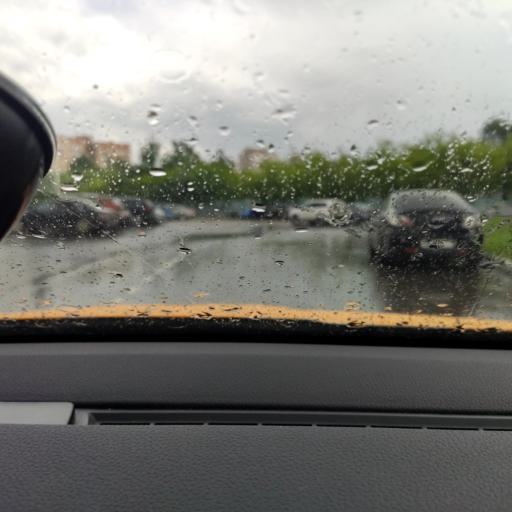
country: RU
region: Moskovskaya
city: Stupino
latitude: 54.8914
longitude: 38.0691
